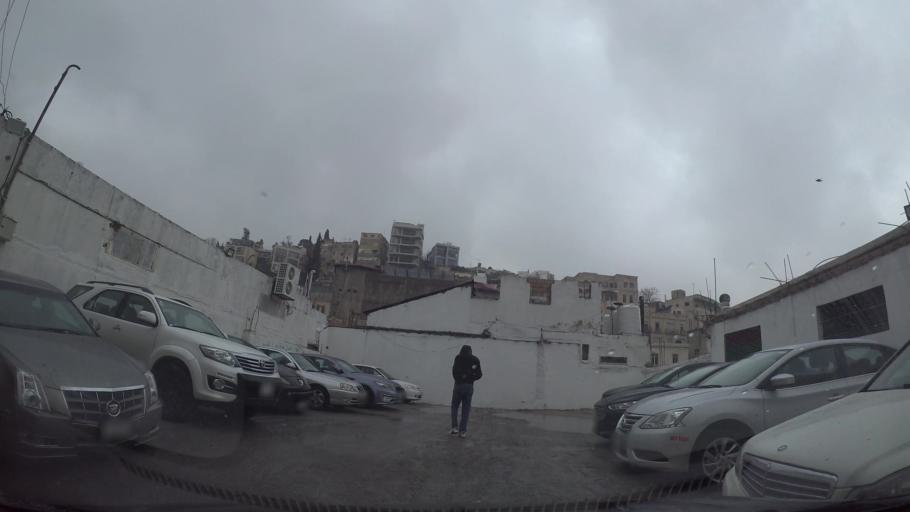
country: JO
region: Amman
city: Amman
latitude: 31.9527
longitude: 35.9309
